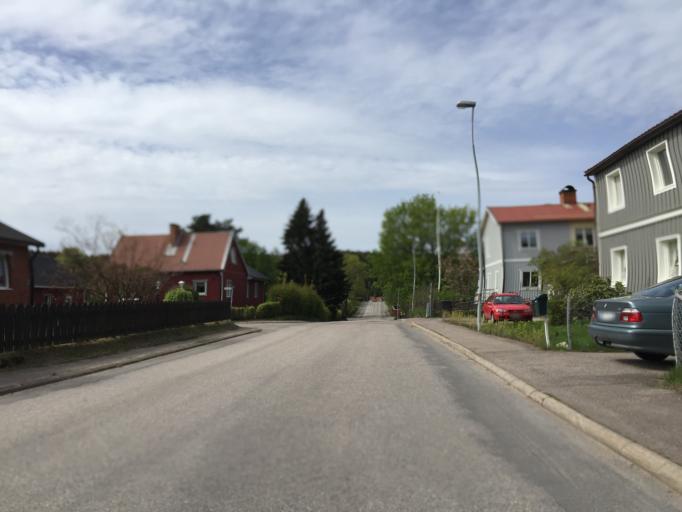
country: SE
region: Dalarna
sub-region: Ludvika Kommun
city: Ludvika
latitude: 60.1285
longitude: 15.1807
